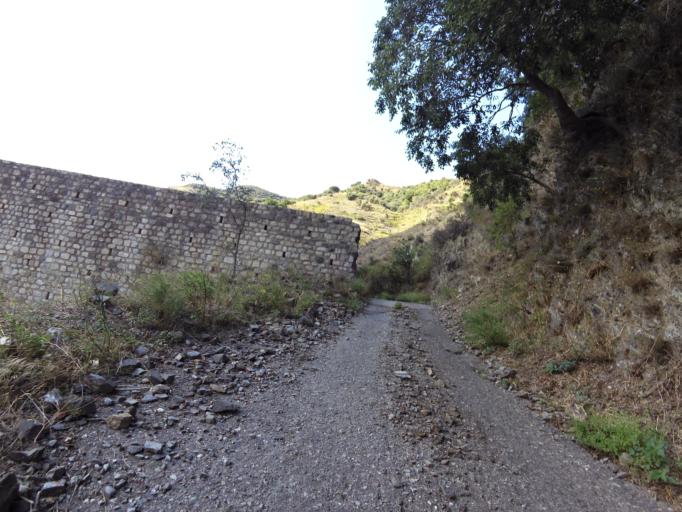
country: IT
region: Calabria
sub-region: Provincia di Reggio Calabria
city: Bivongi
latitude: 38.4923
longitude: 16.4550
